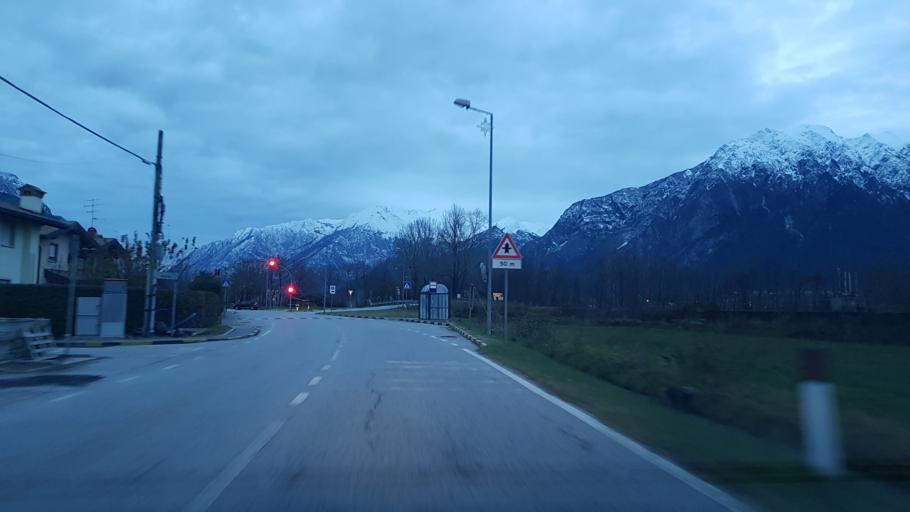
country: IT
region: Friuli Venezia Giulia
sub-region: Provincia di Udine
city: Gemona
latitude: 46.2752
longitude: 13.0995
